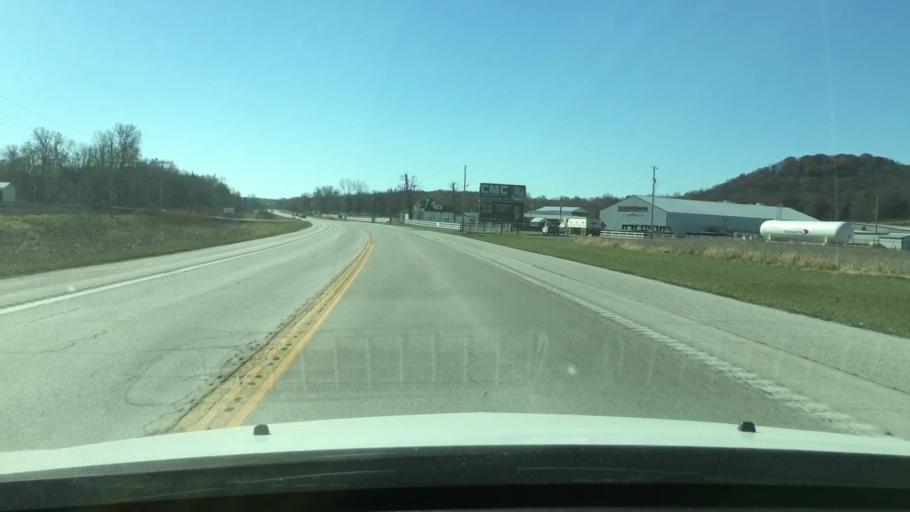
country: US
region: Missouri
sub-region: Pike County
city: Louisiana
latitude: 39.4109
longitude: -91.1023
